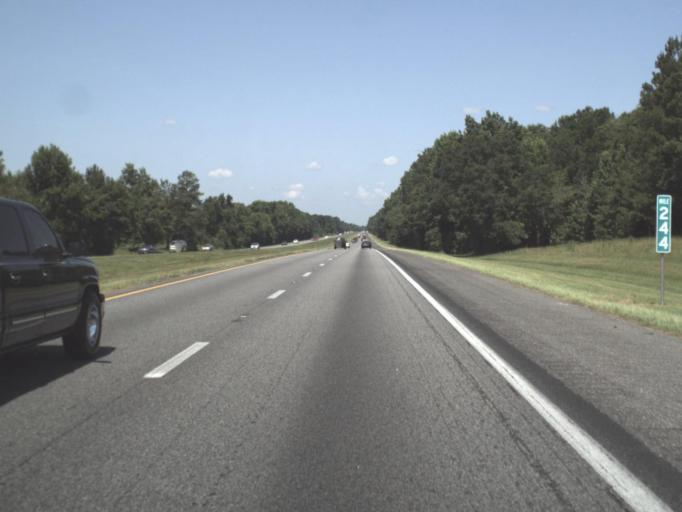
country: US
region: Florida
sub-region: Madison County
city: Madison
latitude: 30.4308
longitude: -83.5804
